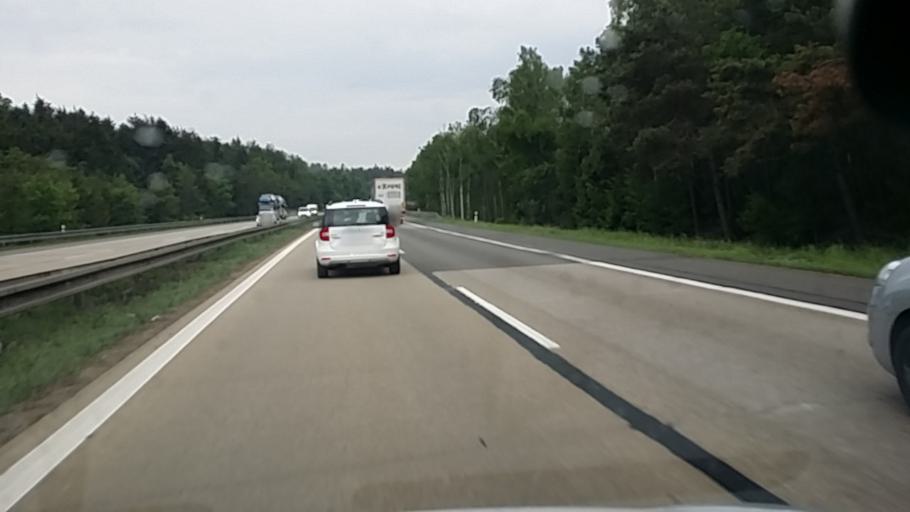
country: CZ
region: South Moravian
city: Zbraslav
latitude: 49.2588
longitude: 16.3142
